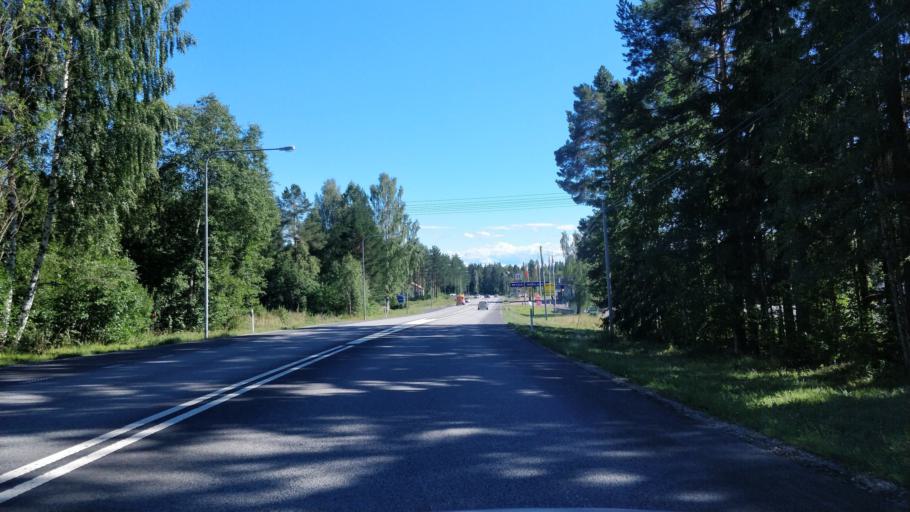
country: SE
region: Dalarna
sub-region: Faluns Kommun
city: Bjursas
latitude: 60.7275
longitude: 15.4458
